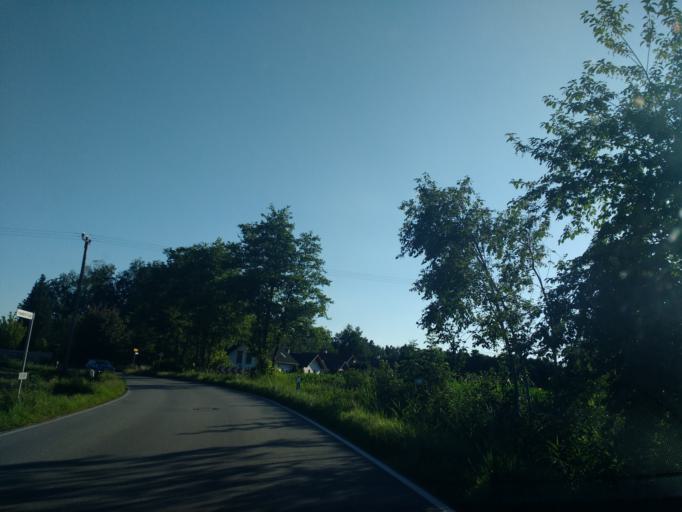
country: DE
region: Bavaria
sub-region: Upper Bavaria
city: Muehldorf
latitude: 48.2213
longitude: 12.5213
